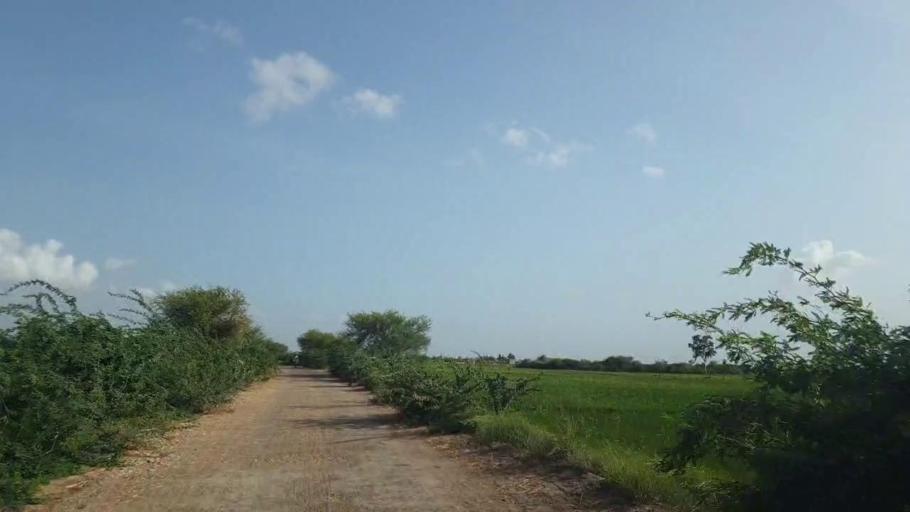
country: PK
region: Sindh
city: Kadhan
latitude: 24.6190
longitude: 69.0958
